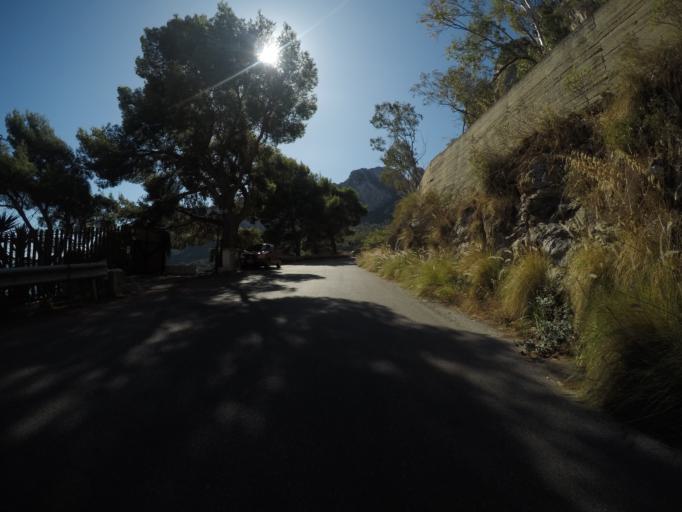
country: IT
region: Sicily
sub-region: Palermo
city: Palermo
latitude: 38.1934
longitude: 13.3390
